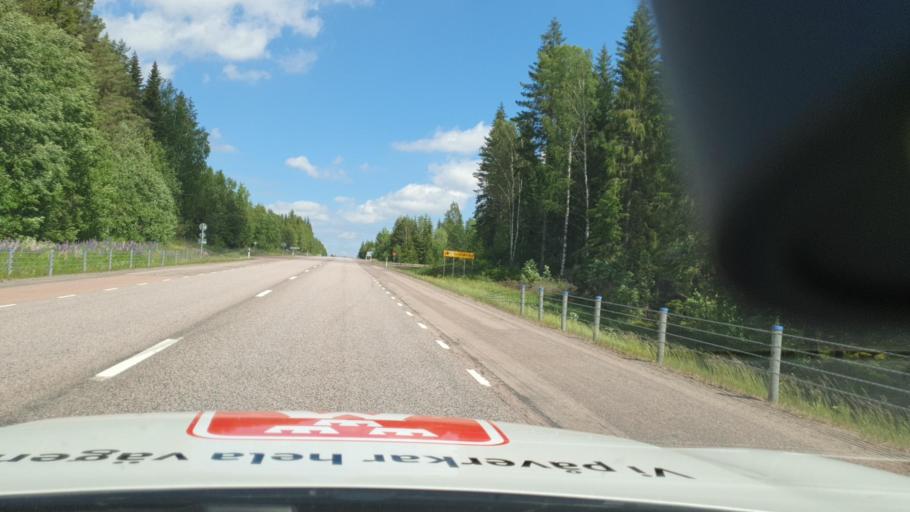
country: SE
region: Vaermland
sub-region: Filipstads Kommun
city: Filipstad
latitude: 59.6996
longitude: 14.1140
